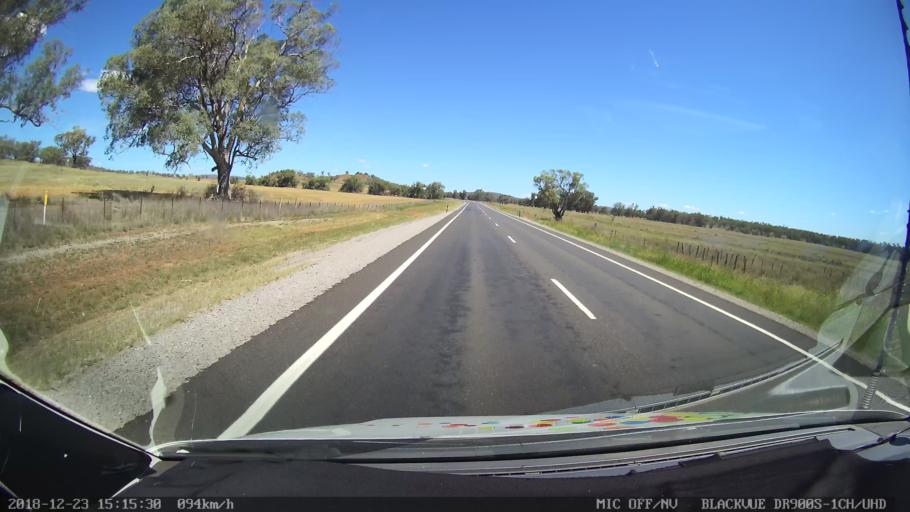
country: AU
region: New South Wales
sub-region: Tamworth Municipality
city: Manilla
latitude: -30.7865
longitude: 150.7431
